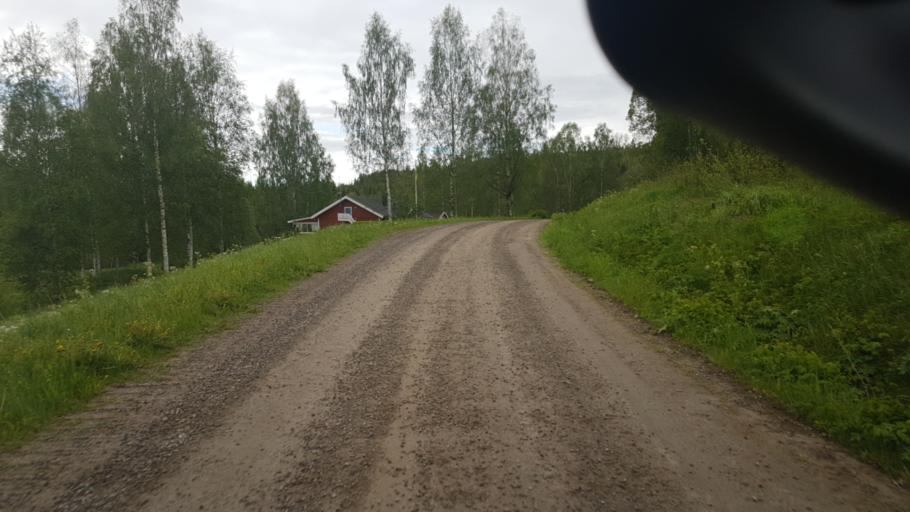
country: SE
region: Vaermland
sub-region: Eda Kommun
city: Amotfors
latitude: 59.7888
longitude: 12.4287
